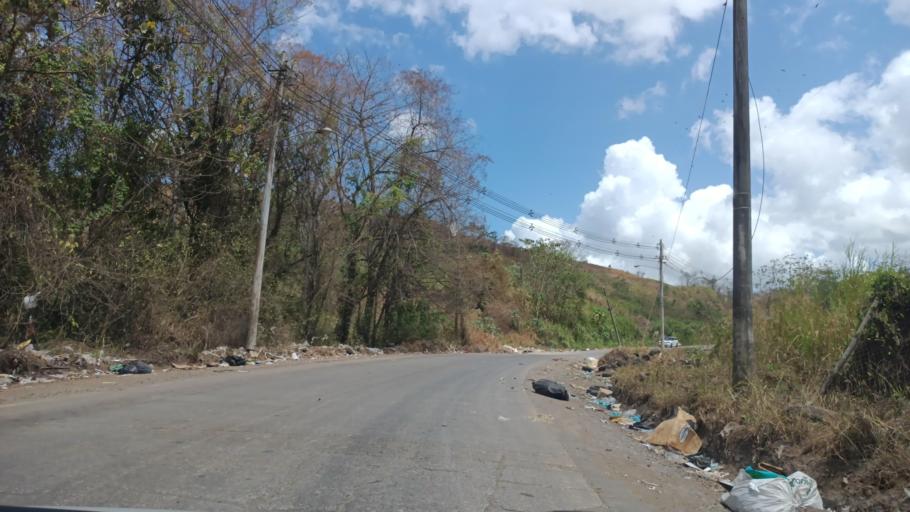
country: PA
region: Panama
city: Las Cumbres
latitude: 9.0490
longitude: -79.5639
